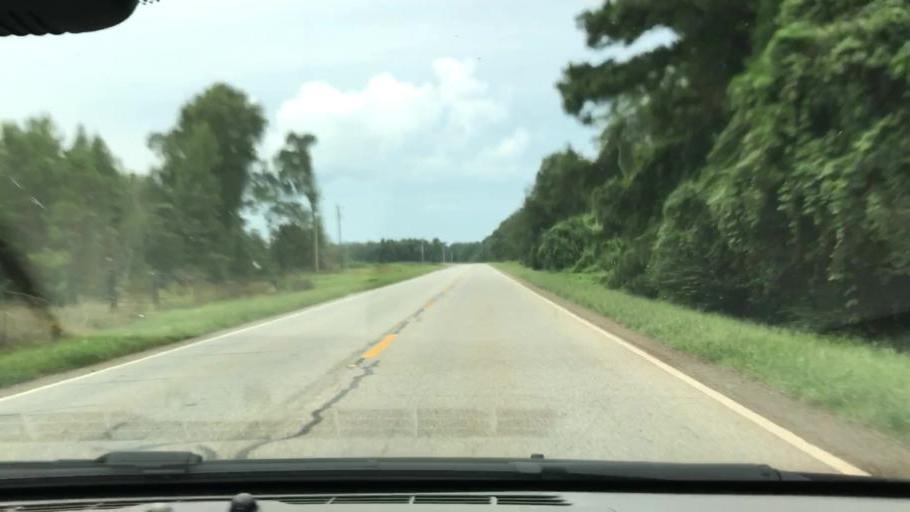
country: US
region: Georgia
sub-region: Early County
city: Blakely
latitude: 31.3165
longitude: -85.0369
